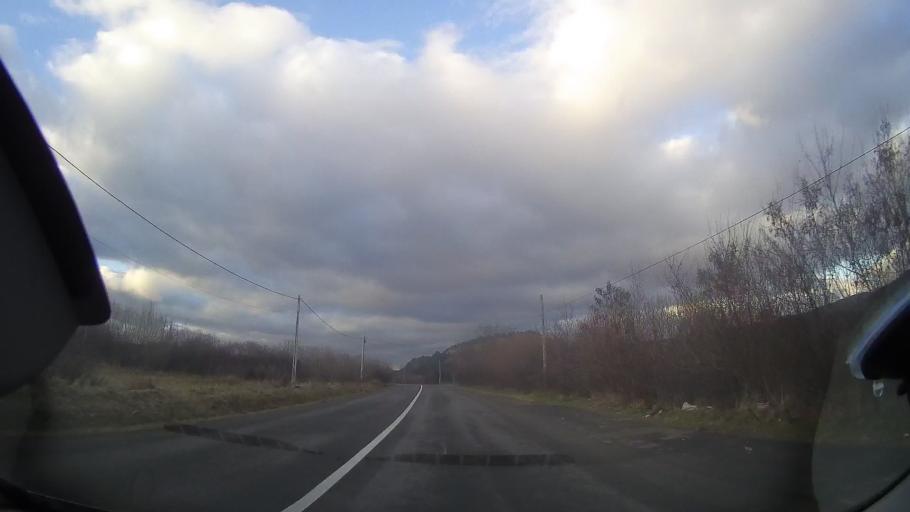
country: RO
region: Cluj
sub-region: Comuna Calatele
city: Calatele
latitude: 46.7816
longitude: 23.0052
